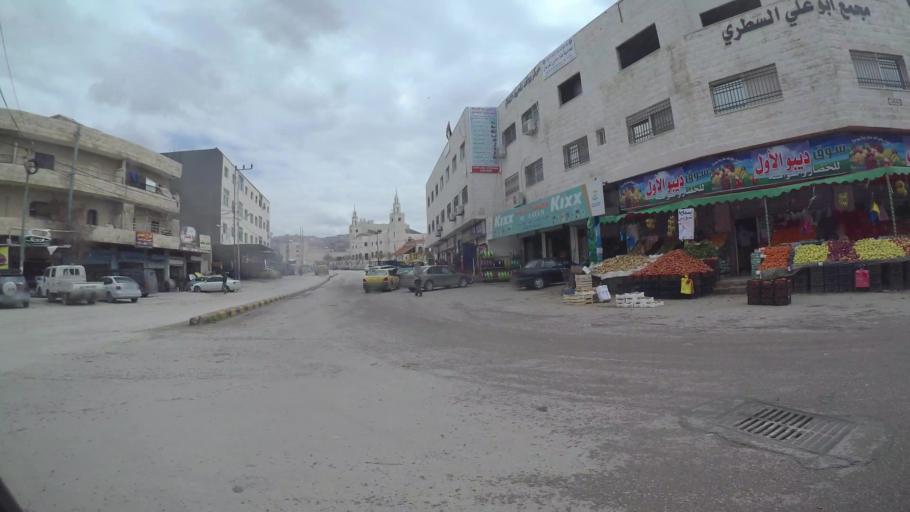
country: JO
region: Amman
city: Al Jubayhah
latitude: 32.0545
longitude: 35.8342
